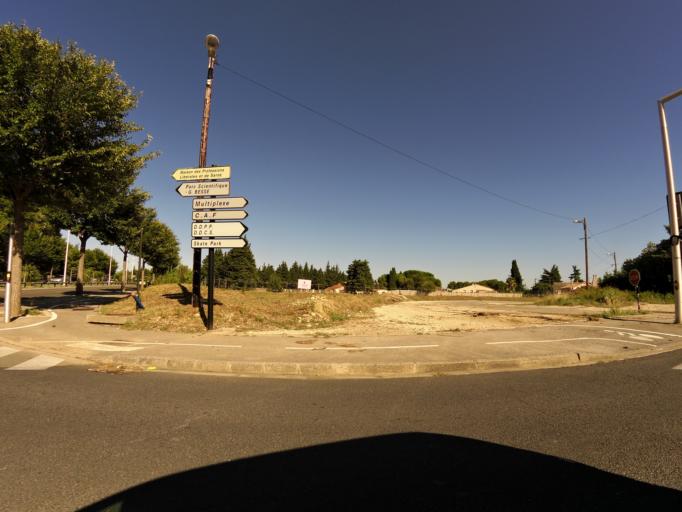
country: FR
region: Languedoc-Roussillon
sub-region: Departement du Gard
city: Nimes
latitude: 43.8181
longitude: 4.3663
